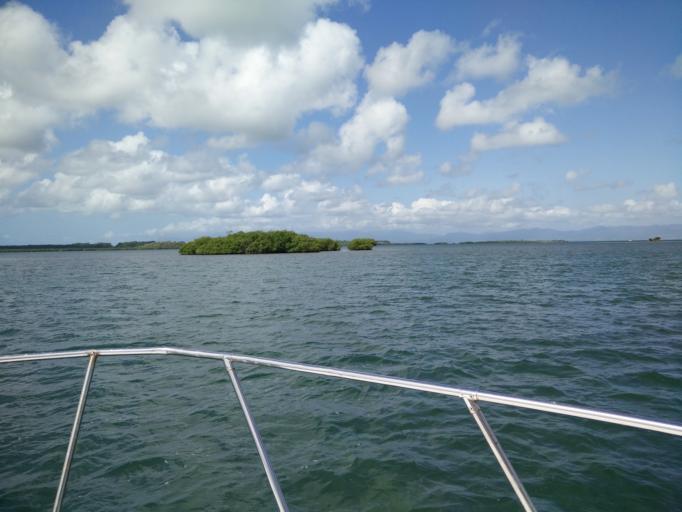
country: GP
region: Guadeloupe
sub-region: Guadeloupe
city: Petit-Canal
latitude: 16.3664
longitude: -61.5014
